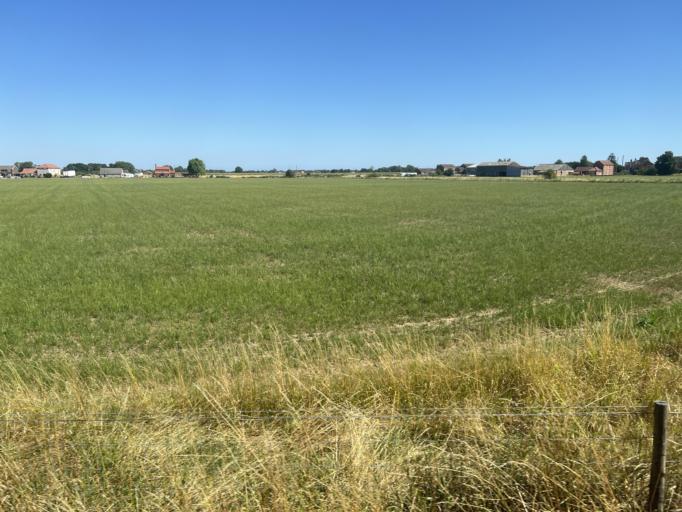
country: GB
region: England
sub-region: Lincolnshire
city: Wainfleet All Saints
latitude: 53.1091
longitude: 0.2262
